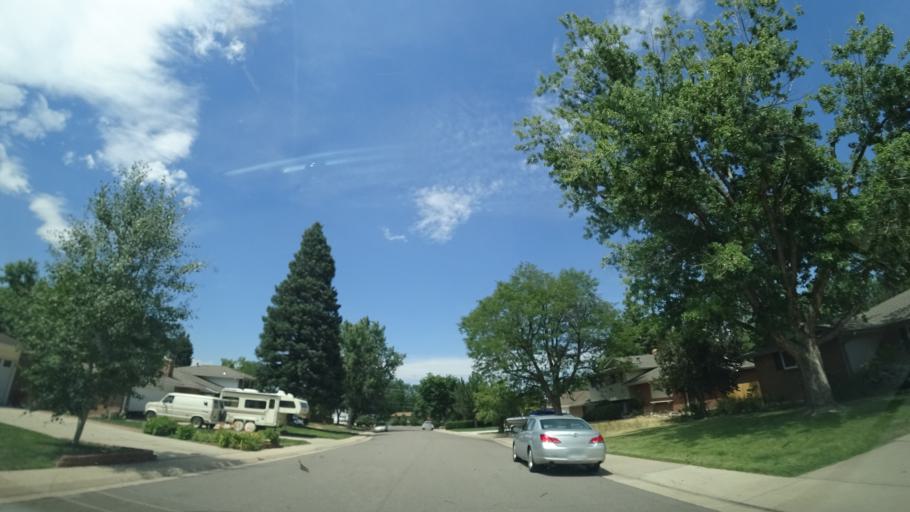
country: US
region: Colorado
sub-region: Jefferson County
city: Lakewood
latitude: 39.6954
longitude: -105.0967
